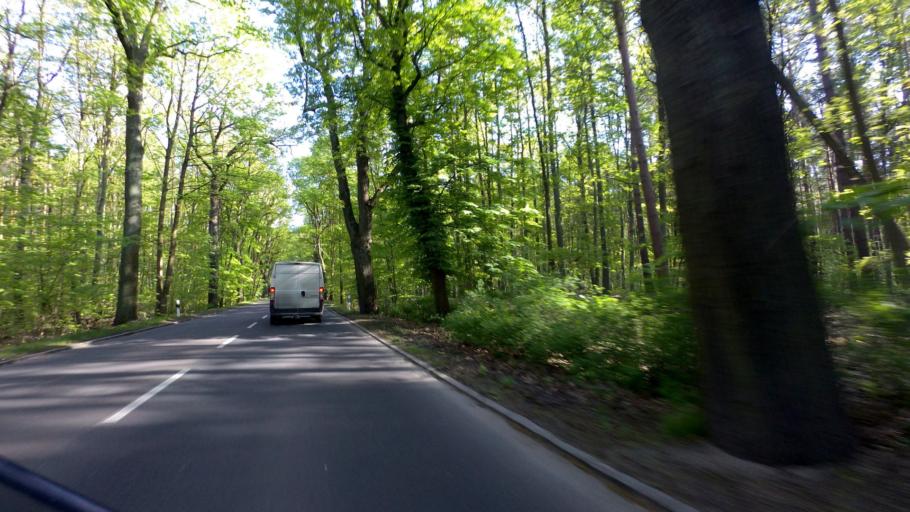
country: DE
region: Berlin
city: Frohnau
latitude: 52.6552
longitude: 13.2908
